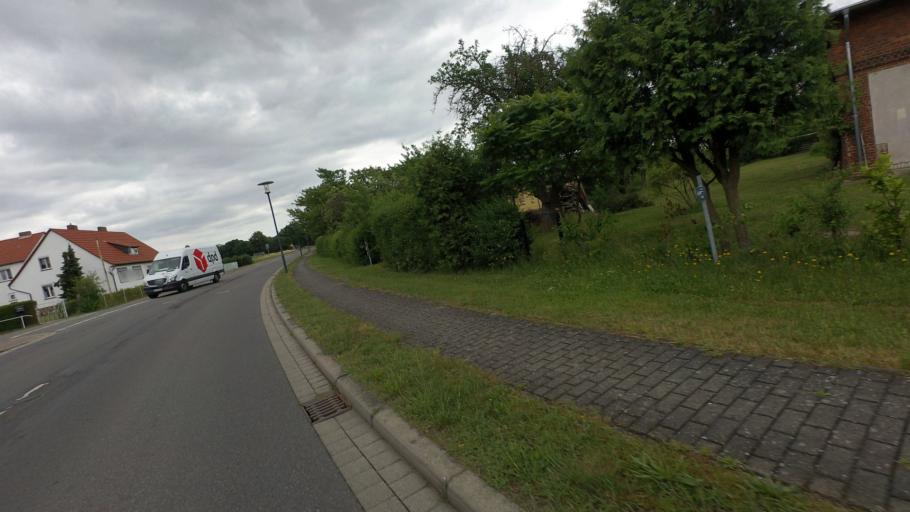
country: DE
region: Brandenburg
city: Crinitz
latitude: 51.8065
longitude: 13.8227
